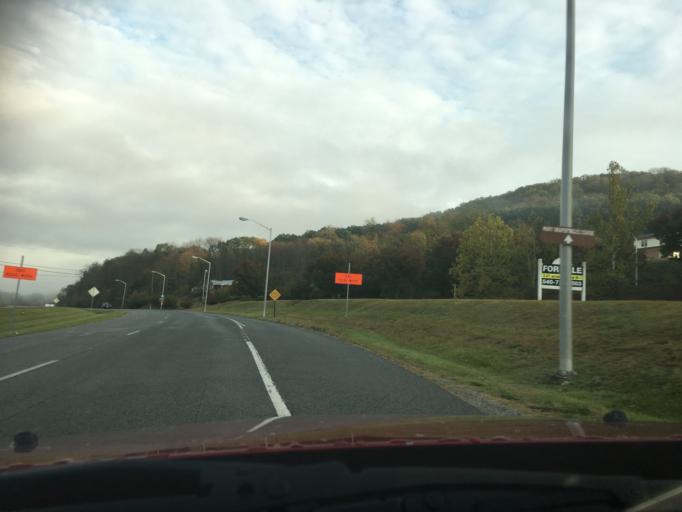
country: US
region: Virginia
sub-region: City of Radford
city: Radford
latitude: 37.0945
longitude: -80.5785
